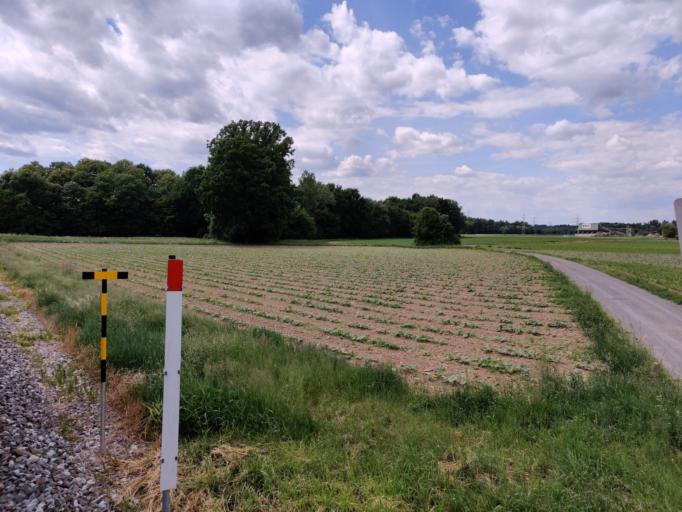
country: AT
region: Styria
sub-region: Politischer Bezirk Leibnitz
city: Spielfeld
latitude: 46.7182
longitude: 15.6667
